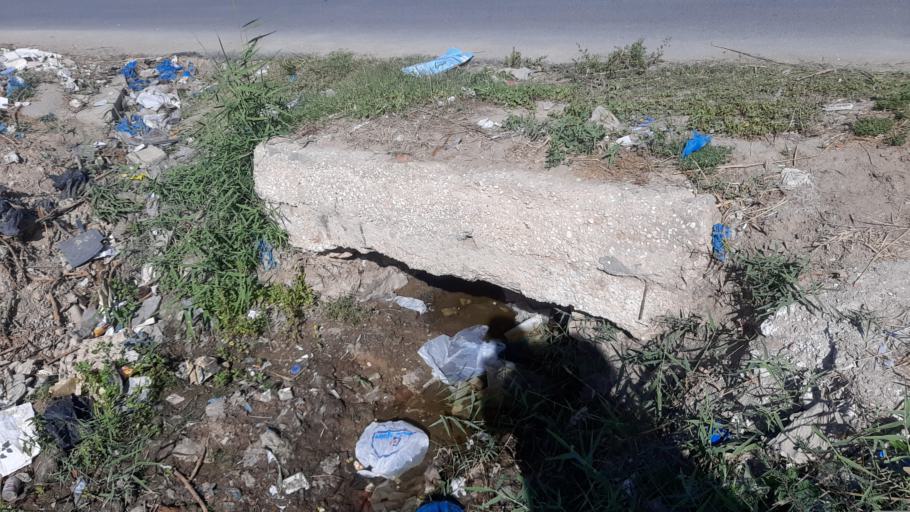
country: TN
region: Qabis
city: Gabes
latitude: 33.8679
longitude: 10.1033
